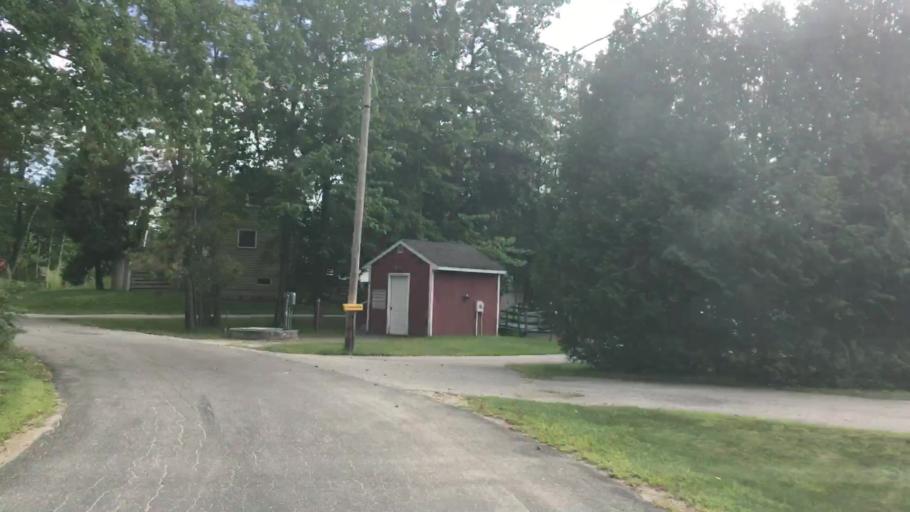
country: US
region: Maine
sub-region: Androscoggin County
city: Sabattus
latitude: 44.1204
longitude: -70.0906
